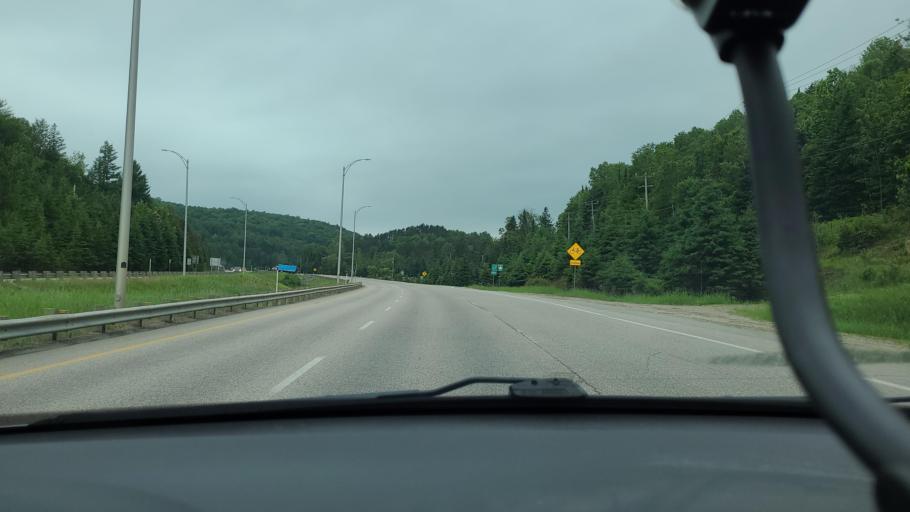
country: CA
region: Quebec
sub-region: Laurentides
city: Mont-Tremblant
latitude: 46.1348
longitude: -74.6198
